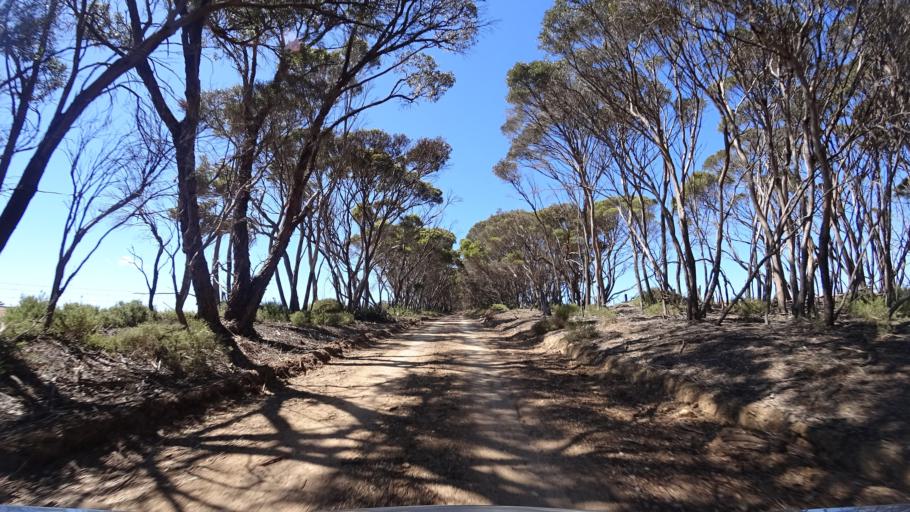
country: AU
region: South Australia
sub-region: Kangaroo Island
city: Kingscote
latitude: -35.7410
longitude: 137.7209
